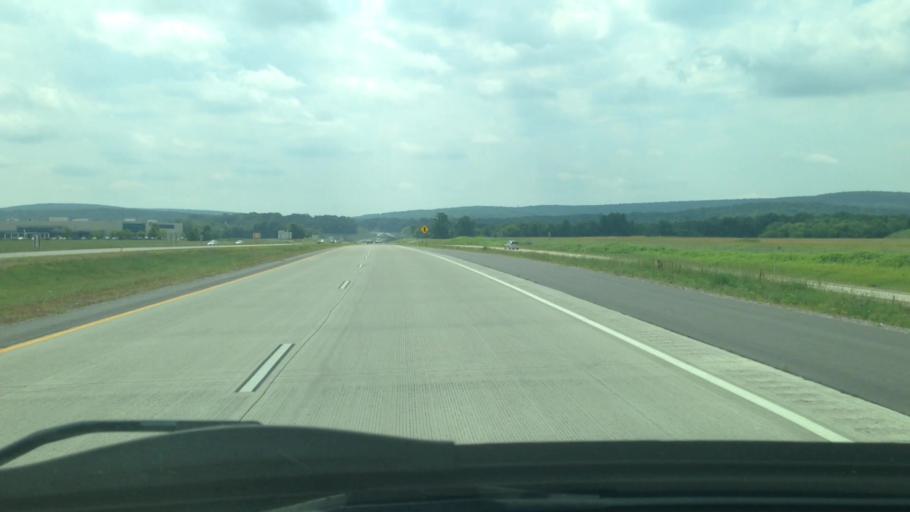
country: US
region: Wisconsin
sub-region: Sauk County
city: West Baraboo
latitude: 43.4594
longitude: -89.7783
